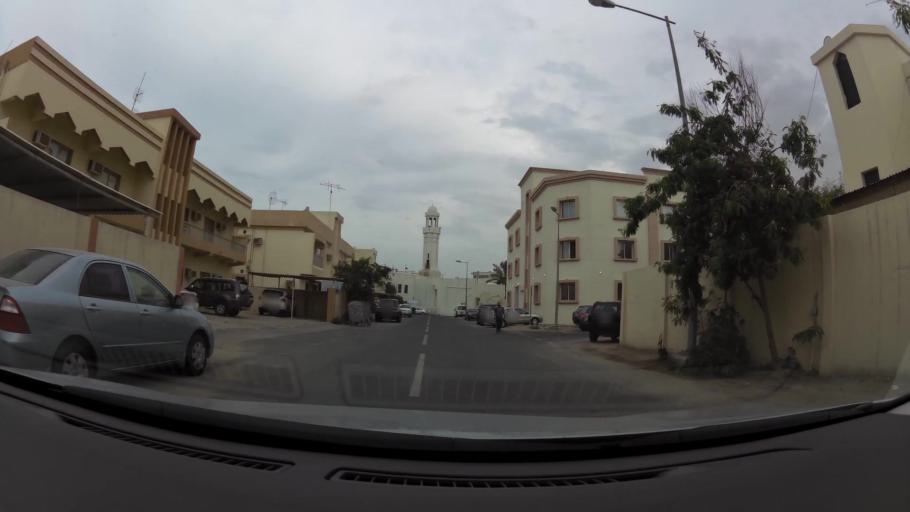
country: QA
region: Baladiyat ad Dawhah
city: Doha
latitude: 25.3112
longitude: 51.4935
